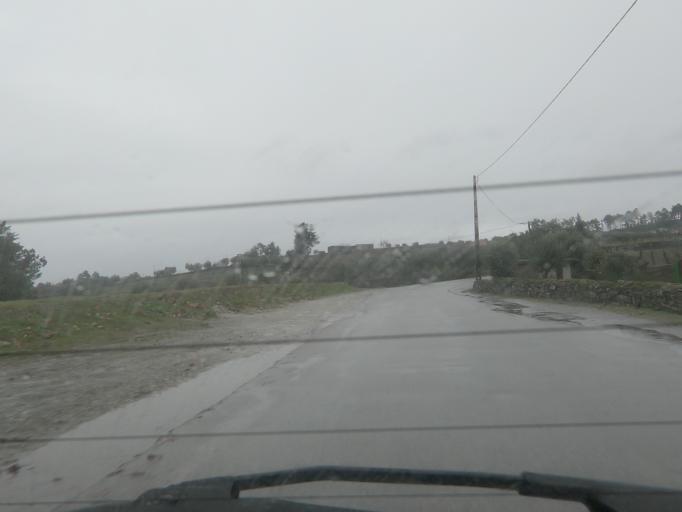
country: PT
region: Vila Real
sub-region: Peso da Regua
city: Peso da Regua
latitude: 41.1983
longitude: -7.7052
